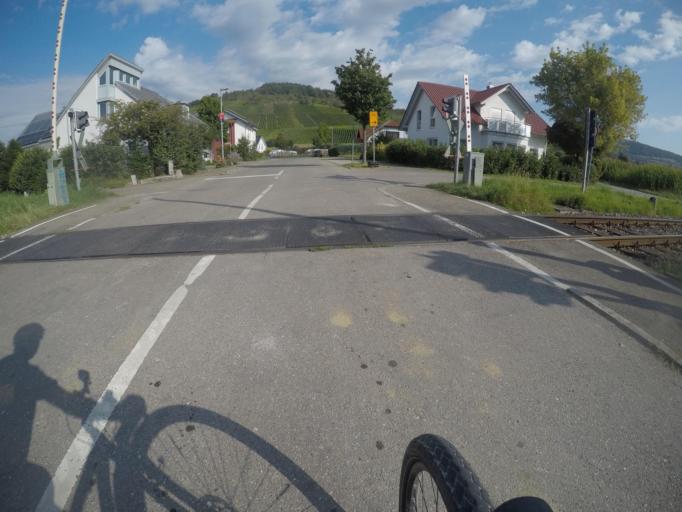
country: DE
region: Baden-Wuerttemberg
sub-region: Tuebingen Region
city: Dettingen an der Erms
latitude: 48.5328
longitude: 9.3153
